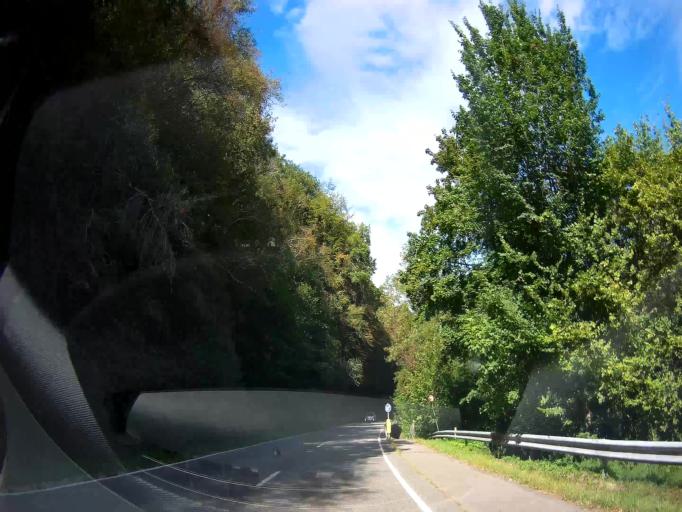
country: BE
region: Wallonia
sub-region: Province du Luxembourg
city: Rendeux
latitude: 50.2118
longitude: 5.5193
